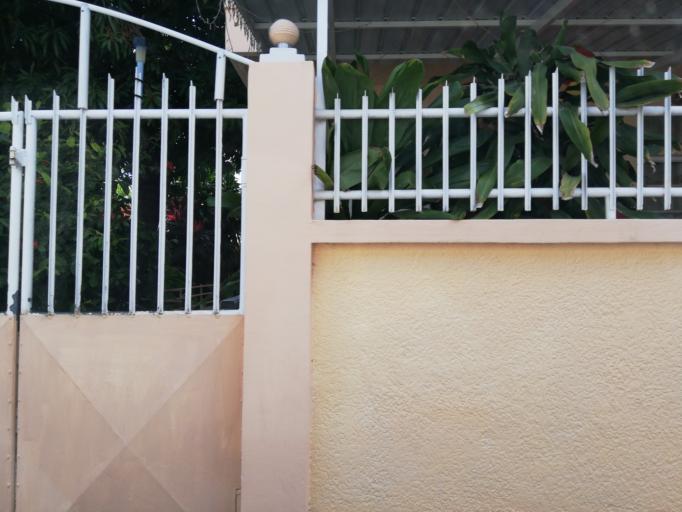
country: MU
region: Port Louis
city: Port Louis
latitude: -20.1625
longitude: 57.4842
